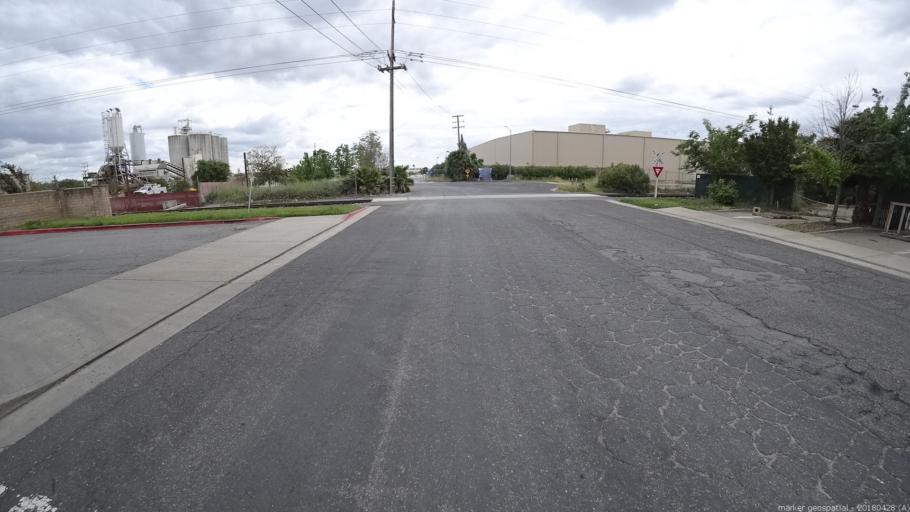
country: US
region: California
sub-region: Yolo County
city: West Sacramento
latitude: 38.5657
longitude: -121.5636
